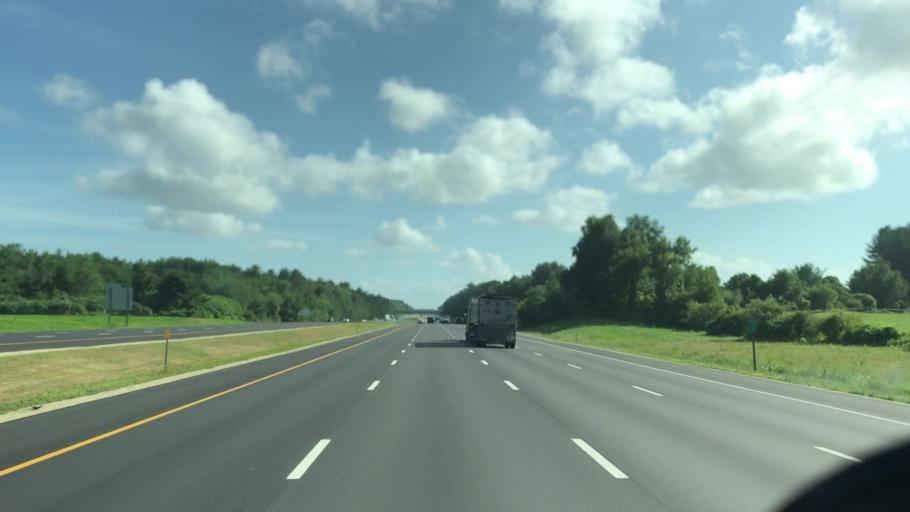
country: US
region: New Hampshire
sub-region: Rockingham County
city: Hampton Falls
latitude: 42.9318
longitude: -70.8640
